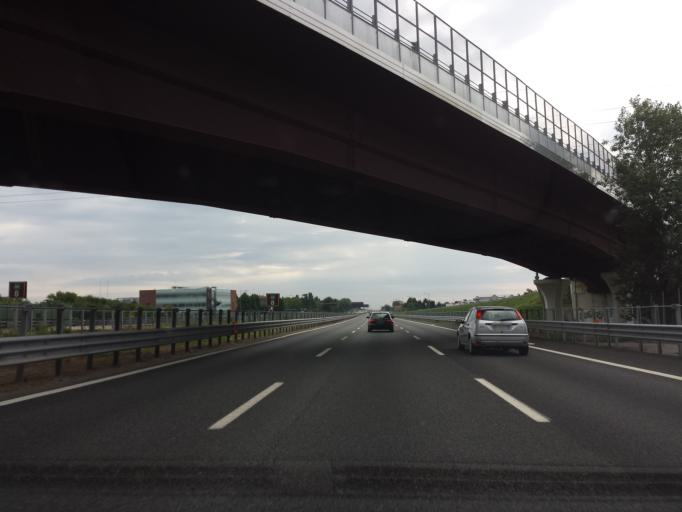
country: IT
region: Lombardy
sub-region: Citta metropolitana di Milano
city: Lainate
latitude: 45.5743
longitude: 9.0110
